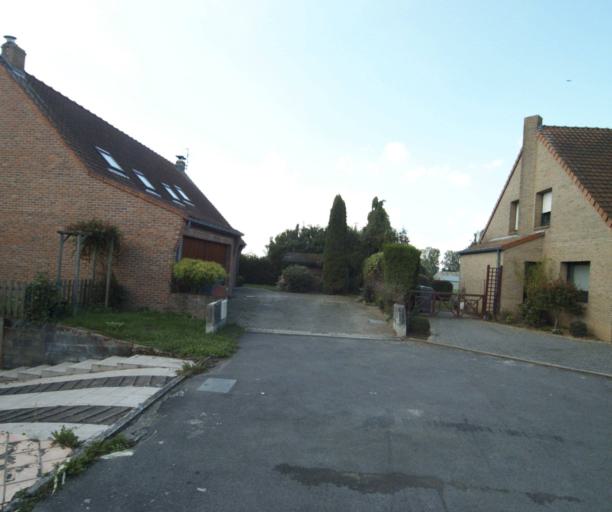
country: FR
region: Nord-Pas-de-Calais
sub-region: Departement du Nord
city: Herlies
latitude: 50.5760
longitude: 2.8512
